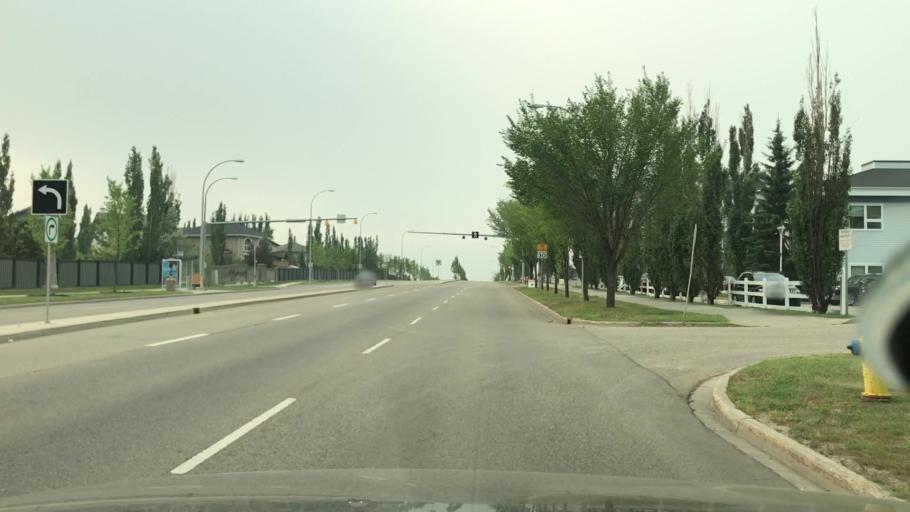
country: CA
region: Alberta
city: Edmonton
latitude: 53.4501
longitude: -113.5656
